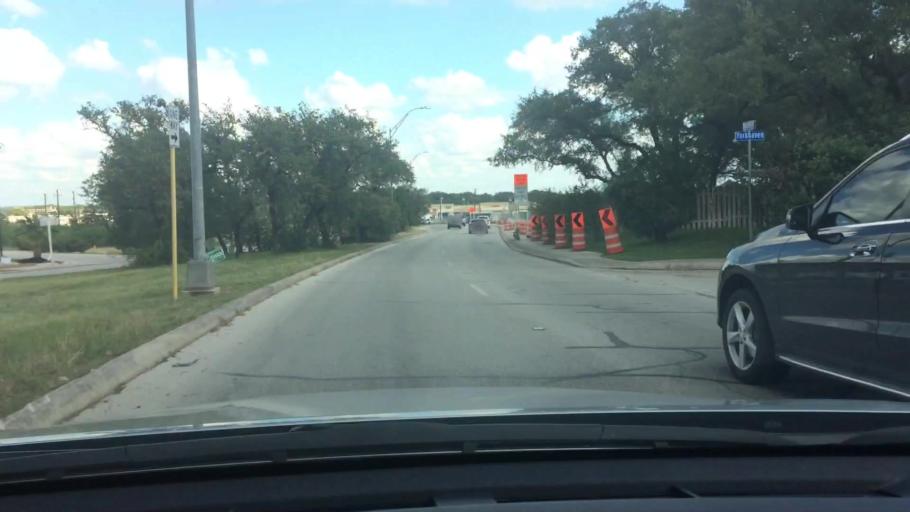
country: US
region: Texas
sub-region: Bexar County
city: Hollywood Park
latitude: 29.6478
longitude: -98.4288
